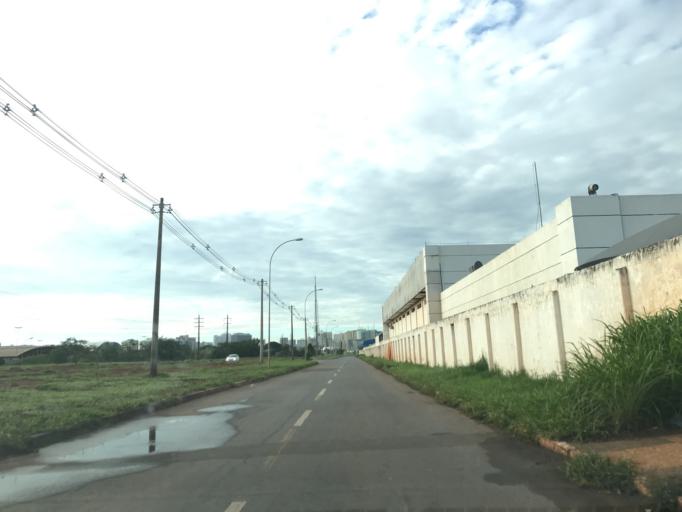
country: BR
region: Federal District
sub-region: Brasilia
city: Brasilia
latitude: -15.7760
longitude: -47.8953
